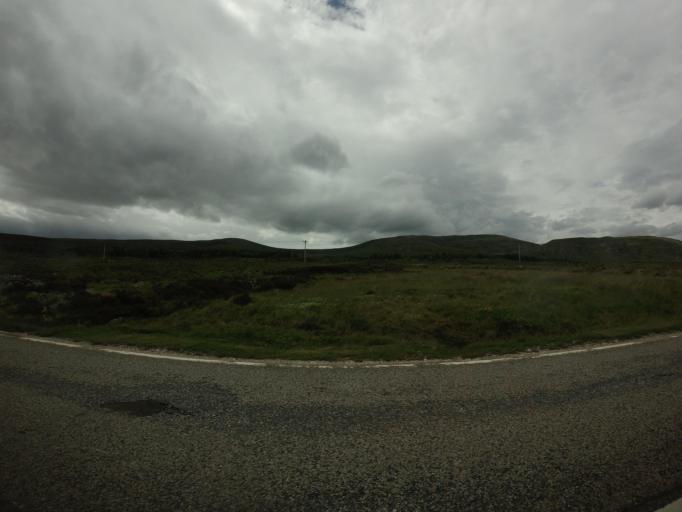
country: GB
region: Scotland
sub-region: Highland
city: Ullapool
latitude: 57.7093
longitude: -4.8364
